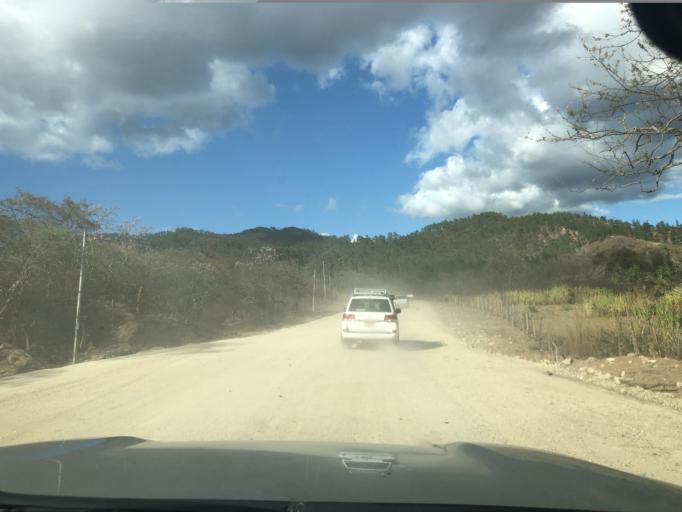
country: NI
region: Nueva Segovia
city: Ocotal
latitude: 13.6647
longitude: -86.6135
